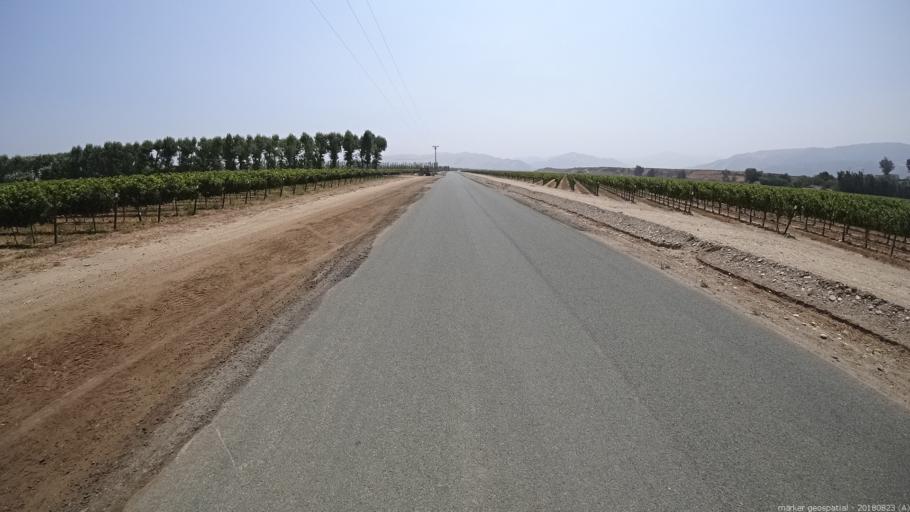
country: US
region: California
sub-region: Monterey County
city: Greenfield
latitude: 36.3455
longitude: -121.2986
